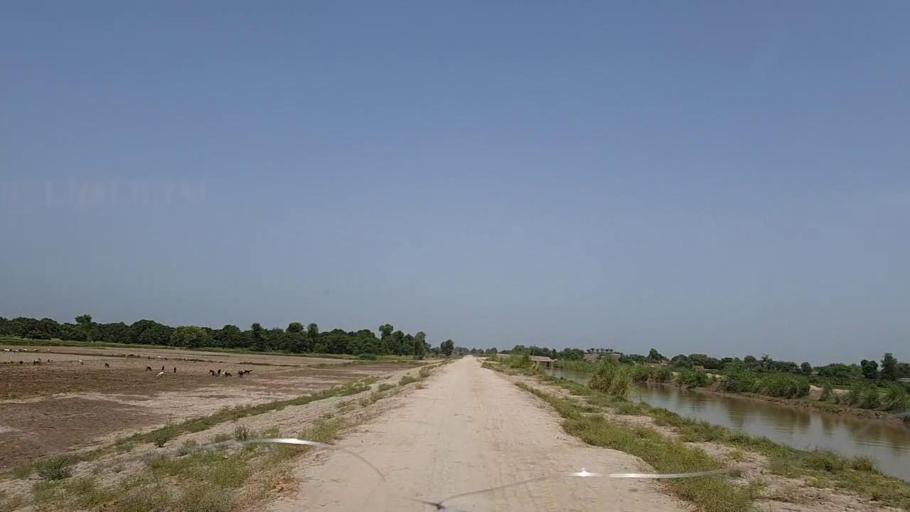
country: PK
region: Sindh
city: Tharu Shah
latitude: 26.9902
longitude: 68.0937
